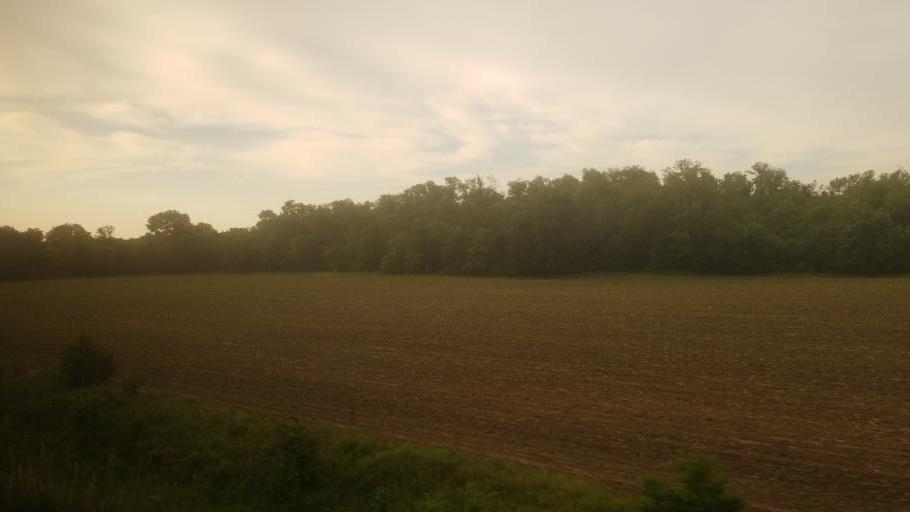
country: US
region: Kansas
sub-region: Osage County
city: Osage City
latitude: 38.5179
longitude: -95.9734
